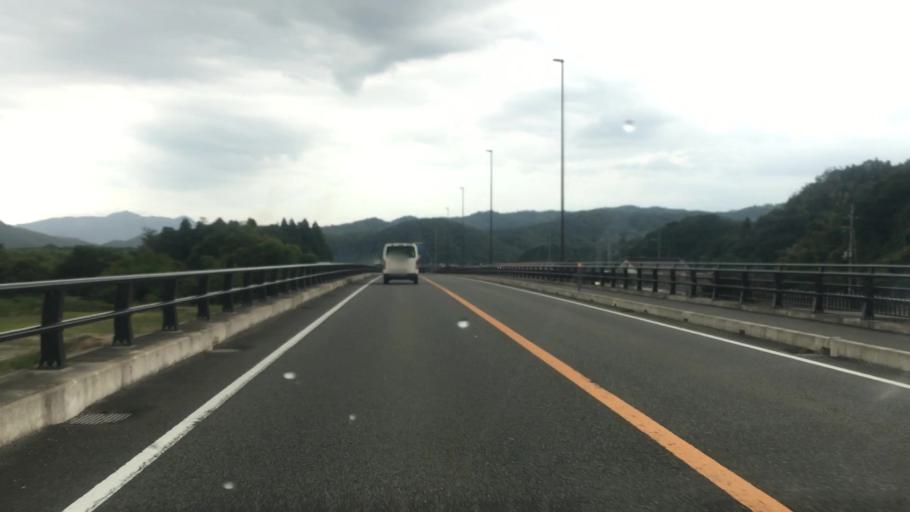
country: JP
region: Hyogo
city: Toyooka
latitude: 35.4774
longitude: 134.7883
